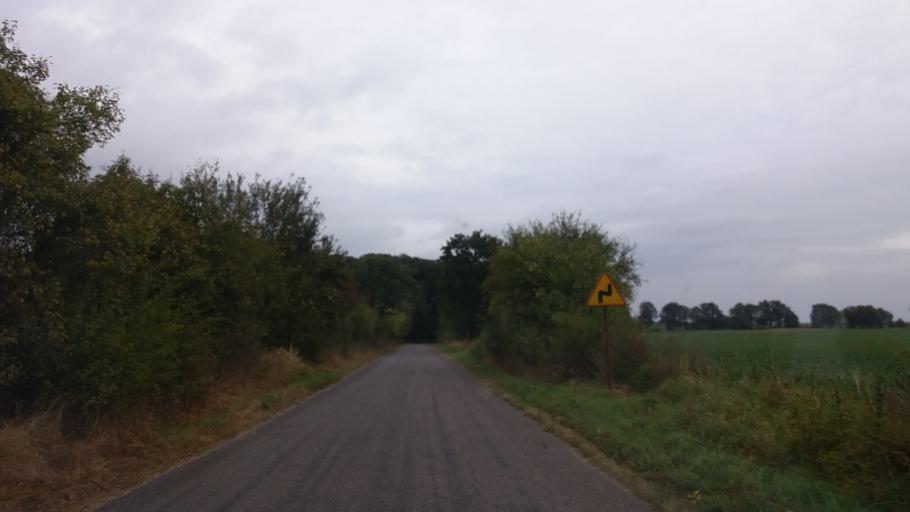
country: PL
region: West Pomeranian Voivodeship
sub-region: Powiat choszczenski
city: Krzecin
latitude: 52.9875
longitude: 15.5191
